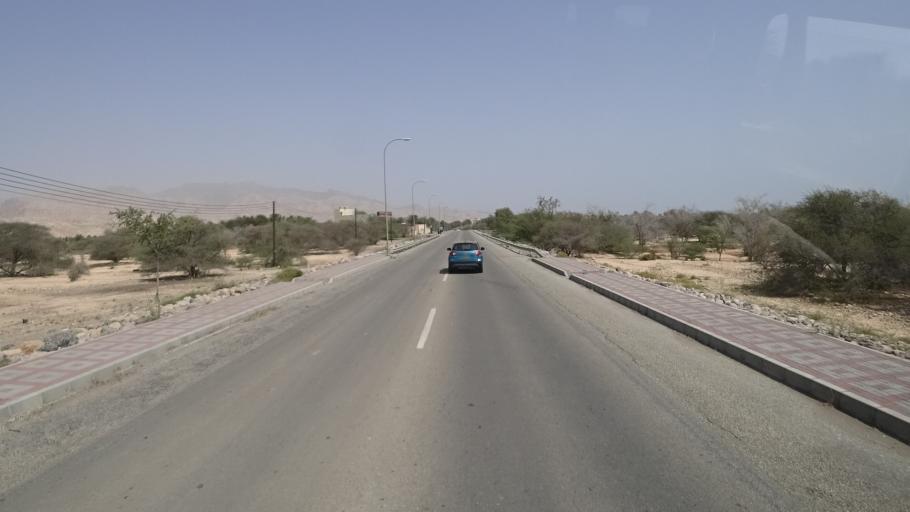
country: OM
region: Muhafazat Masqat
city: Muscat
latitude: 23.2314
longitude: 58.9112
